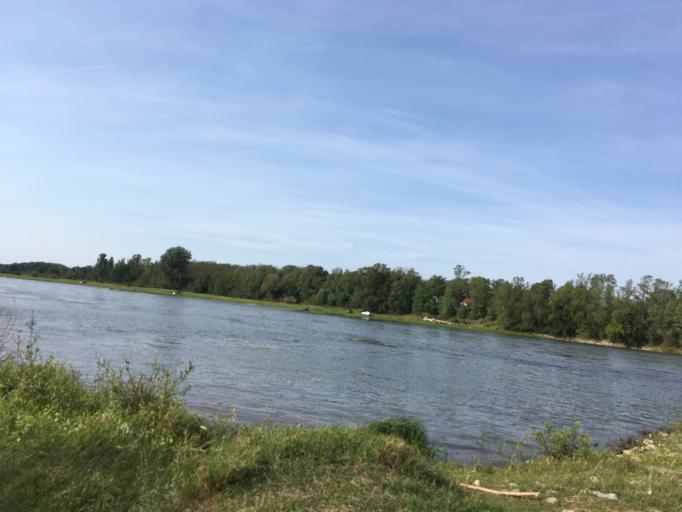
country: DE
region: Brandenburg
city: Ziltendorf
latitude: 52.2618
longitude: 14.6515
